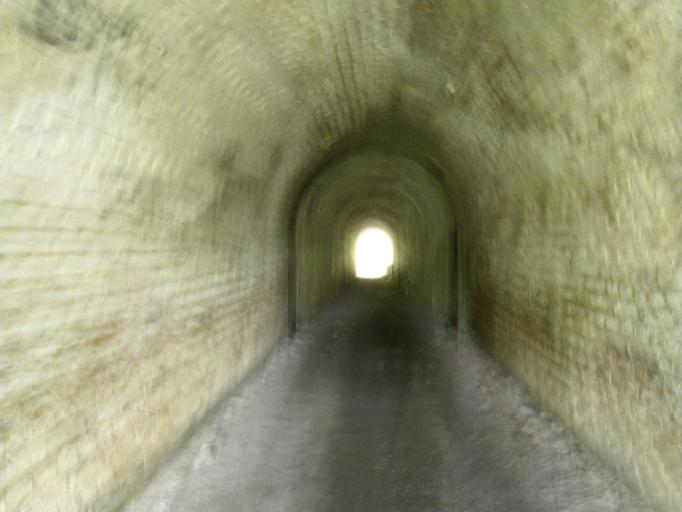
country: BE
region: Wallonia
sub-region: Province du Hainaut
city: Roeulx
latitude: 50.4712
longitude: 4.0501
